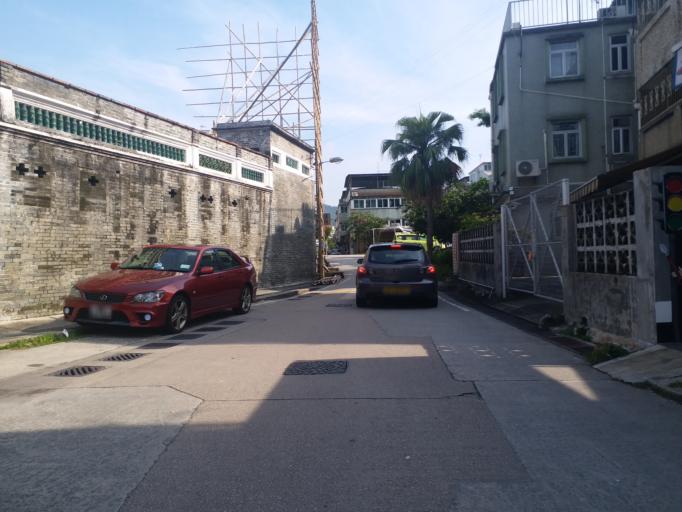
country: HK
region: Yuen Long
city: Yuen Long Kau Hui
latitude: 22.4443
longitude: 114.0073
